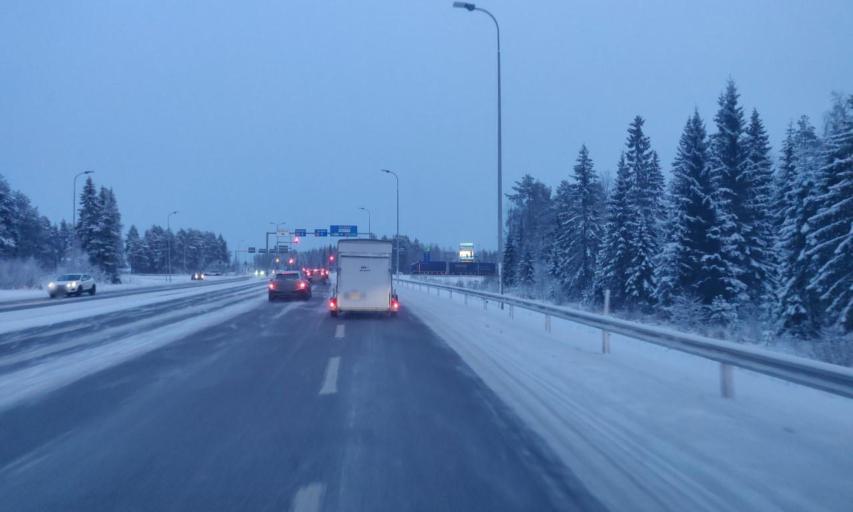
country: FI
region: Northern Ostrobothnia
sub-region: Oulu
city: Kempele
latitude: 64.9815
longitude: 25.5580
